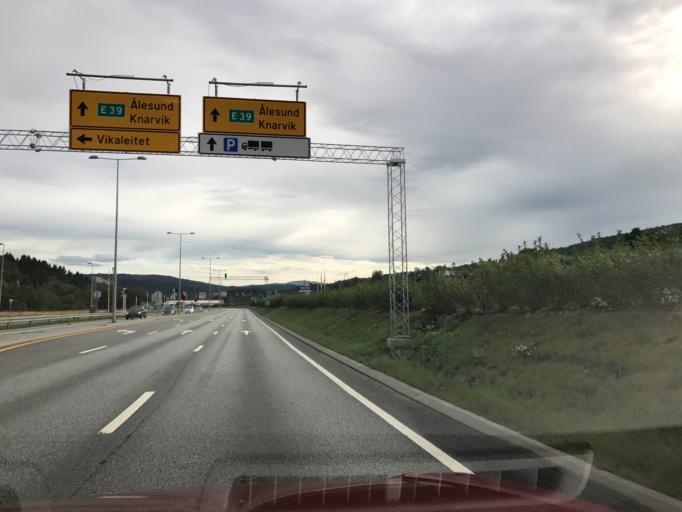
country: NO
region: Hordaland
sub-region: Bergen
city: Hylkje
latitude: 60.4811
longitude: 5.3702
